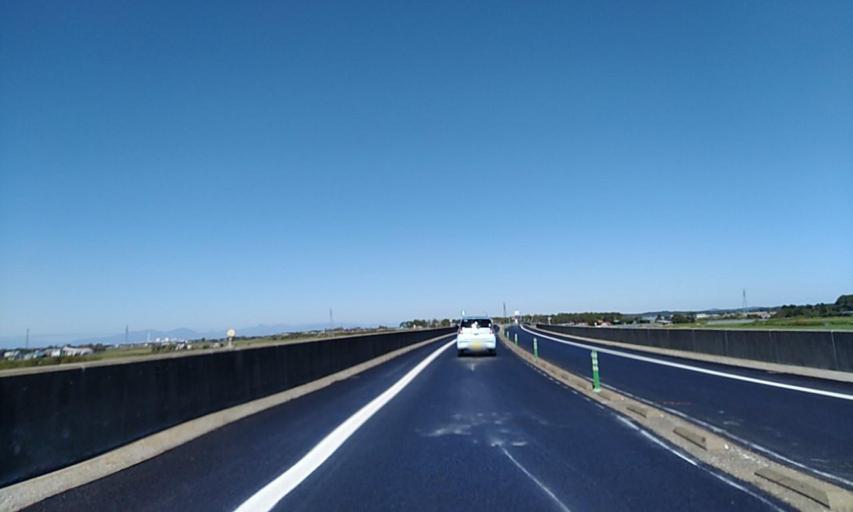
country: JP
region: Hokkaido
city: Tomakomai
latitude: 42.5819
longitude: 141.9464
